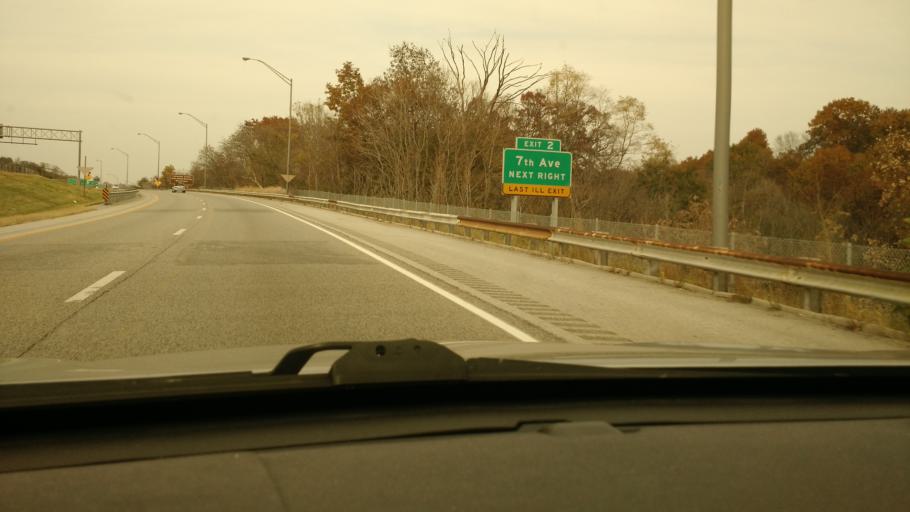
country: US
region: Illinois
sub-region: Rock Island County
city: Moline
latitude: 41.4975
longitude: -90.5067
